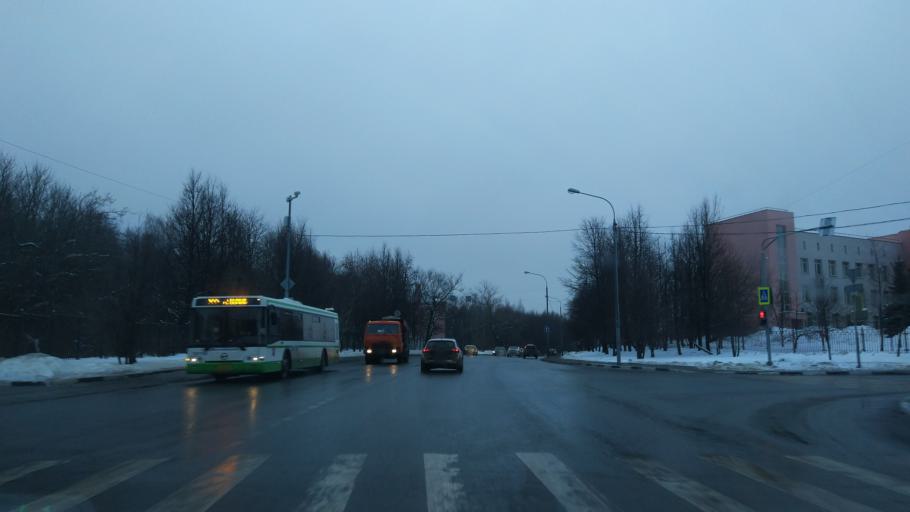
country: RU
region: Moscow
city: Ivanovskoye
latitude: 55.7784
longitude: 37.8192
